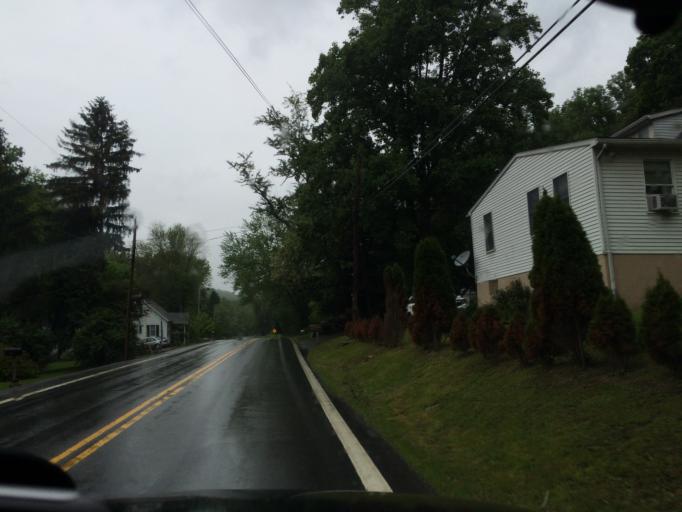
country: US
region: Maryland
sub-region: Frederick County
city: Thurmont
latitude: 39.6530
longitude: -77.4393
